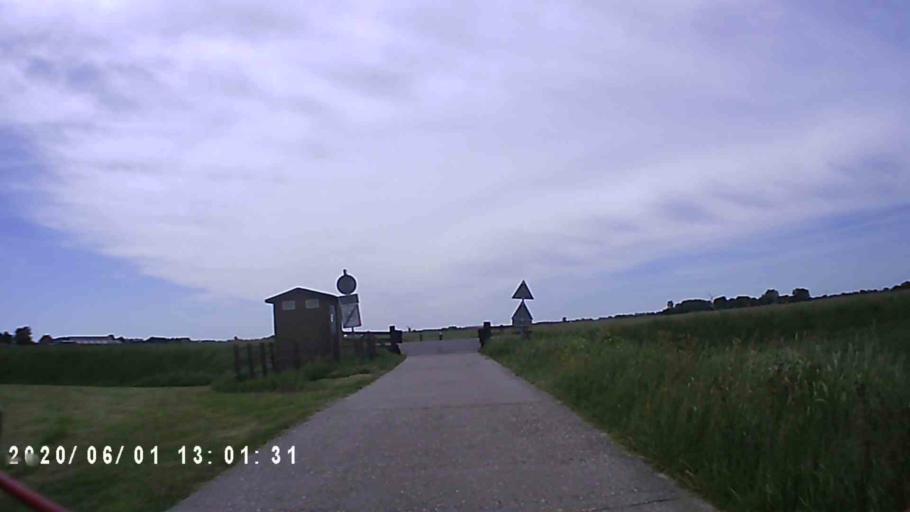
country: NL
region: Friesland
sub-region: Gemeente Franekeradeel
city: Tzum
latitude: 53.1445
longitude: 5.5387
